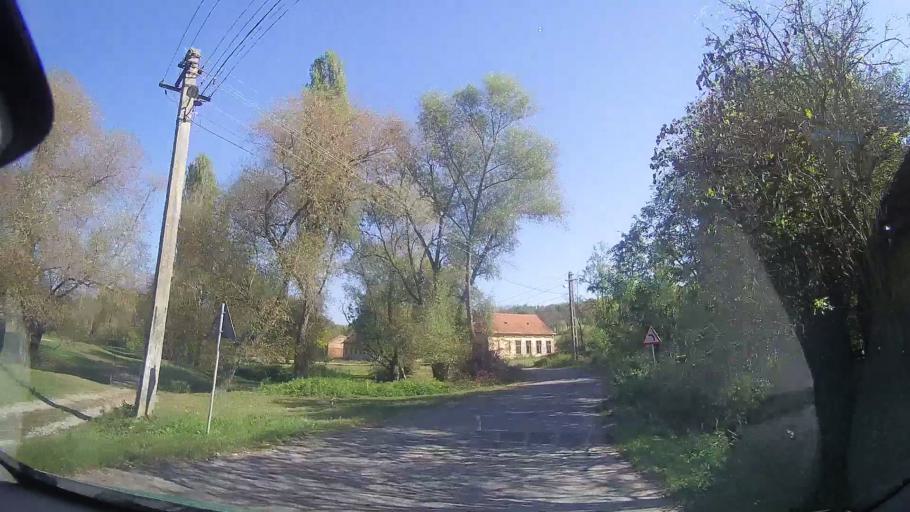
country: RO
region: Timis
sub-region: Comuna Bara
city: Bara
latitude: 45.8933
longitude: 21.9209
